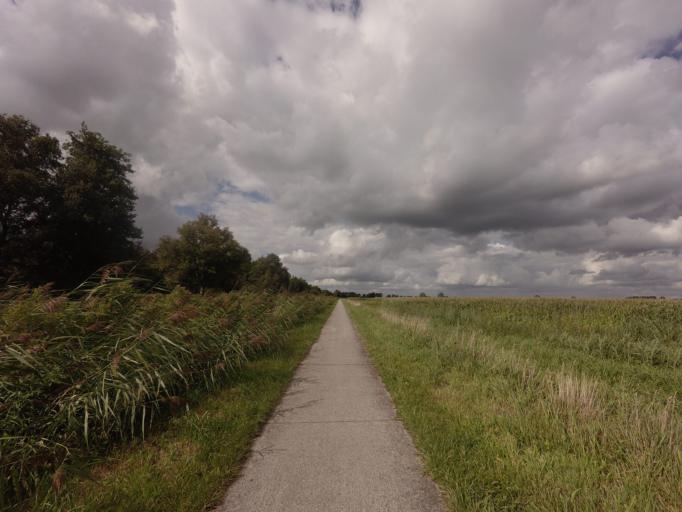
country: NL
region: Overijssel
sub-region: Gemeente Steenwijkerland
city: Giethoorn
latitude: 52.7309
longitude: 6.0516
